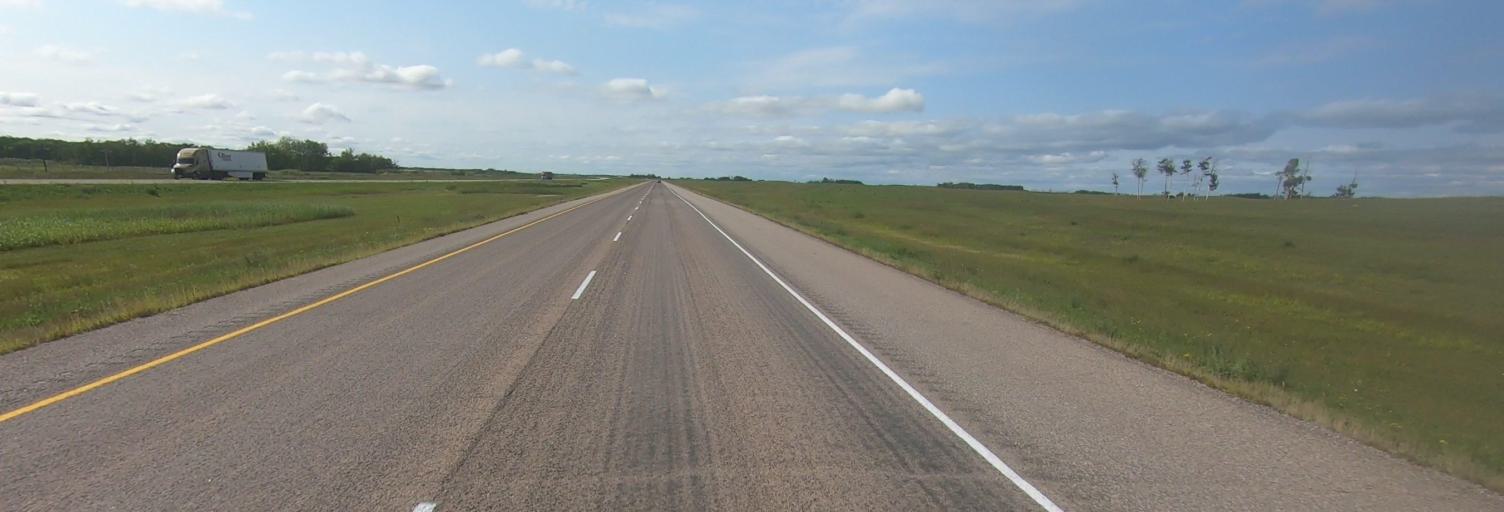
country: CA
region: Manitoba
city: Virden
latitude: 49.9924
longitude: -101.2705
